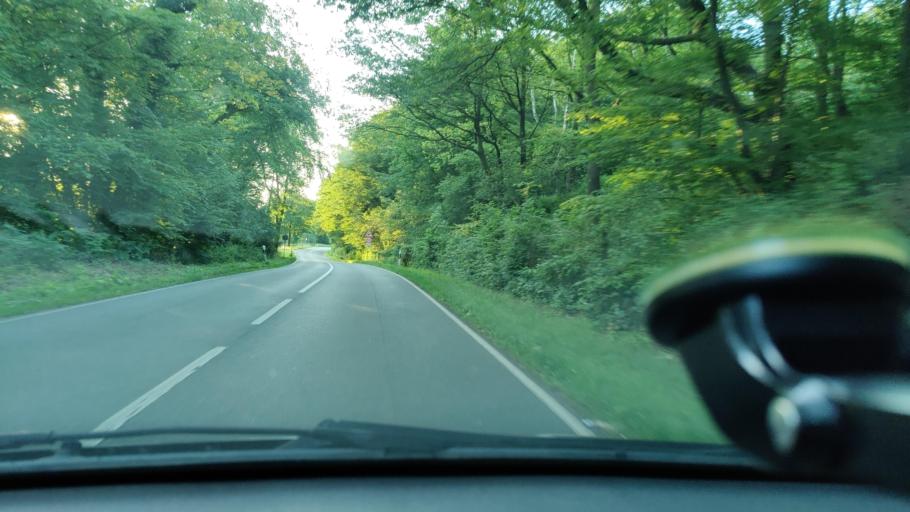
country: DE
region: North Rhine-Westphalia
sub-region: Regierungsbezirk Dusseldorf
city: Kamp-Lintfort
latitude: 51.4831
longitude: 6.5171
